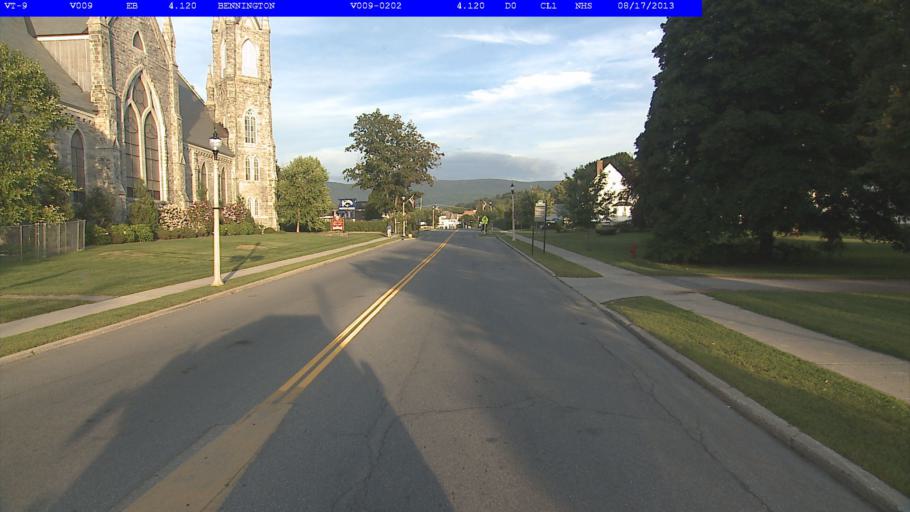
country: US
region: Vermont
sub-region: Bennington County
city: Bennington
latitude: 42.8804
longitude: -73.2018
